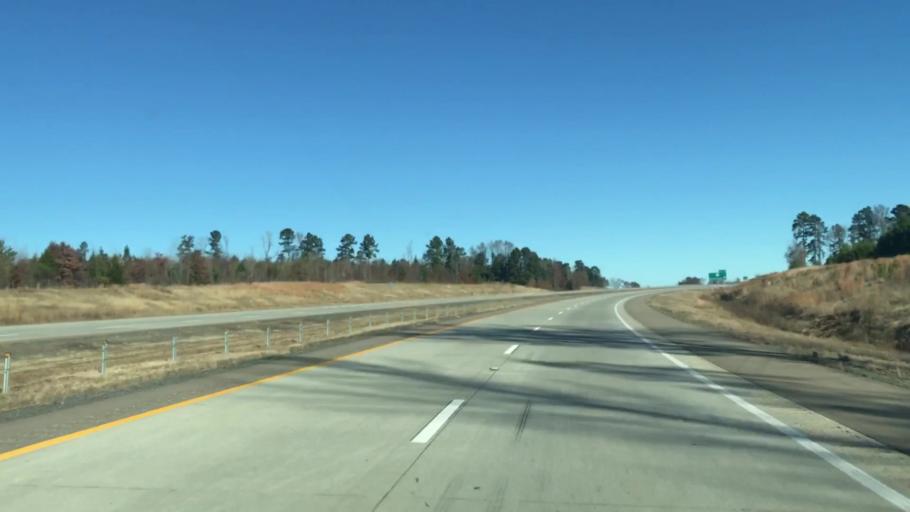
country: US
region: Louisiana
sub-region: Caddo Parish
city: Vivian
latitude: 33.0726
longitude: -93.9049
